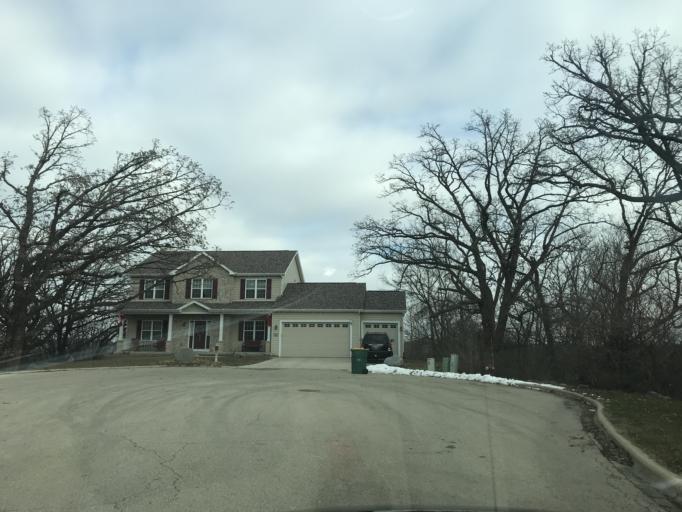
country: US
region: Wisconsin
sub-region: Dane County
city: Monona
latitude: 43.1177
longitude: -89.2911
